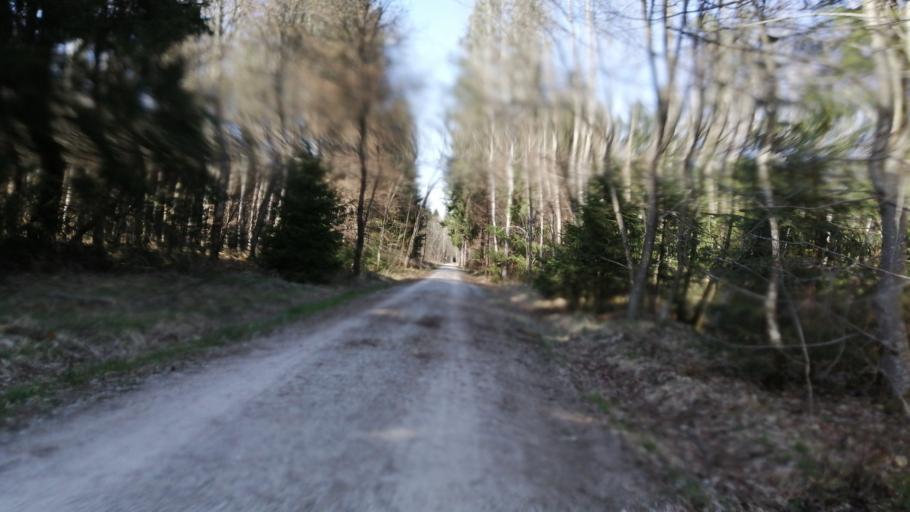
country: DE
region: Bavaria
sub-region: Upper Bavaria
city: Oberhaching
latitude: 48.0006
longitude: 11.6270
